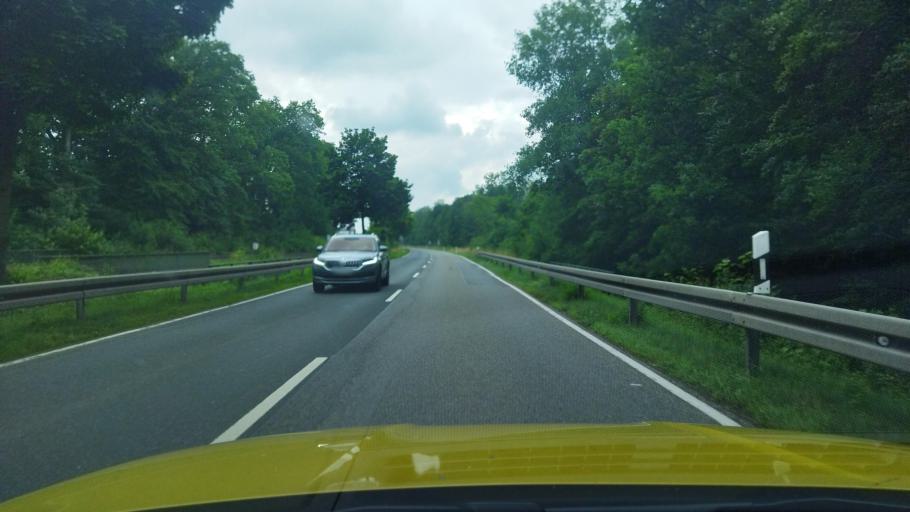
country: DE
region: Bavaria
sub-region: Regierungsbezirk Mittelfranken
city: Gunzenhausen
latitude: 49.1257
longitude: 10.7810
